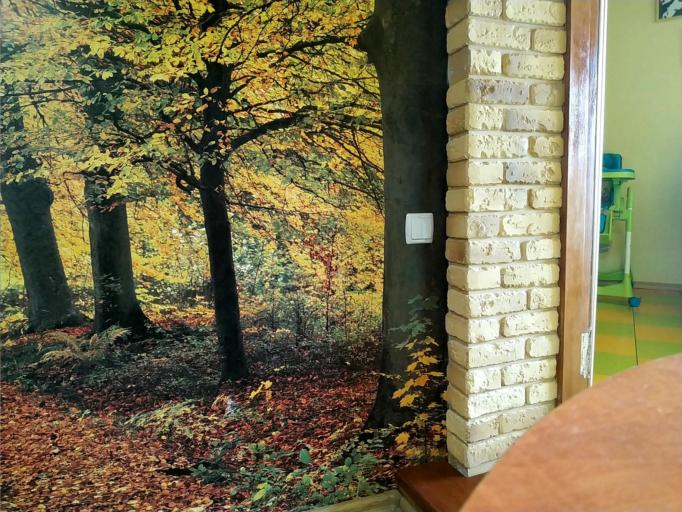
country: RU
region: Smolensk
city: Ozernyy
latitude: 55.4405
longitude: 32.6790
